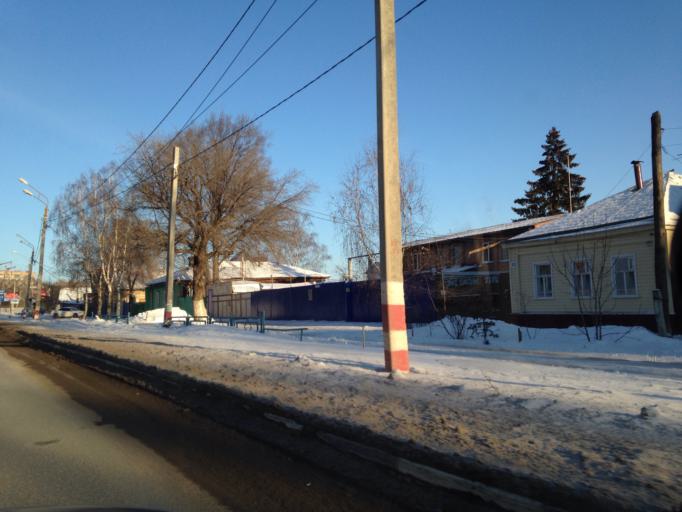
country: RU
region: Ulyanovsk
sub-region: Ulyanovskiy Rayon
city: Ulyanovsk
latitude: 54.3040
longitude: 48.3872
